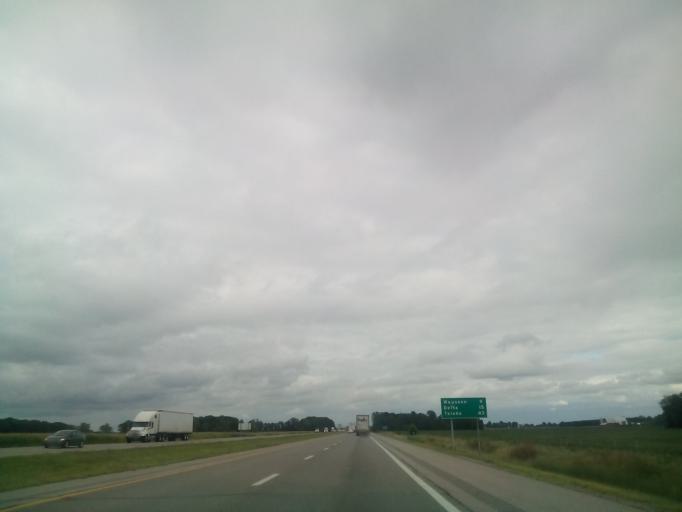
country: US
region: Ohio
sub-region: Fulton County
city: Burlington
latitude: 41.5912
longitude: -84.3046
